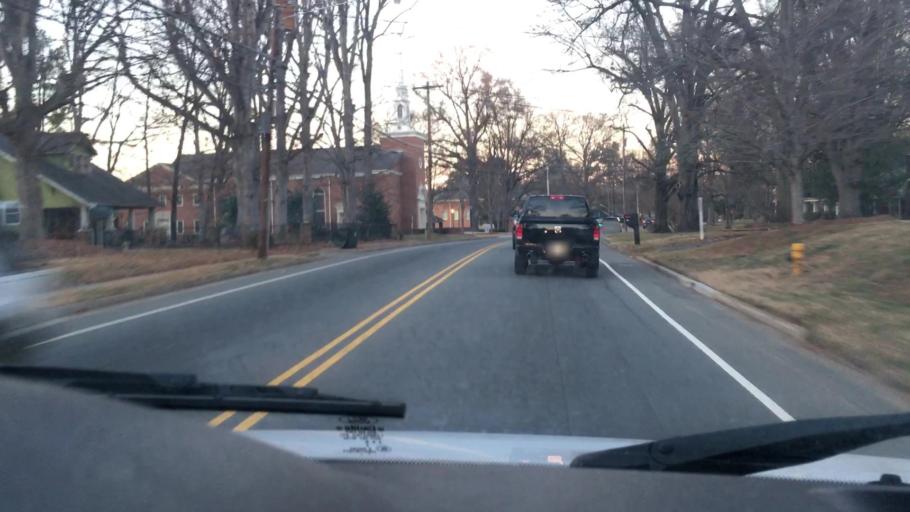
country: US
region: North Carolina
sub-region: Mecklenburg County
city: Huntersville
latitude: 35.4135
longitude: -80.8431
